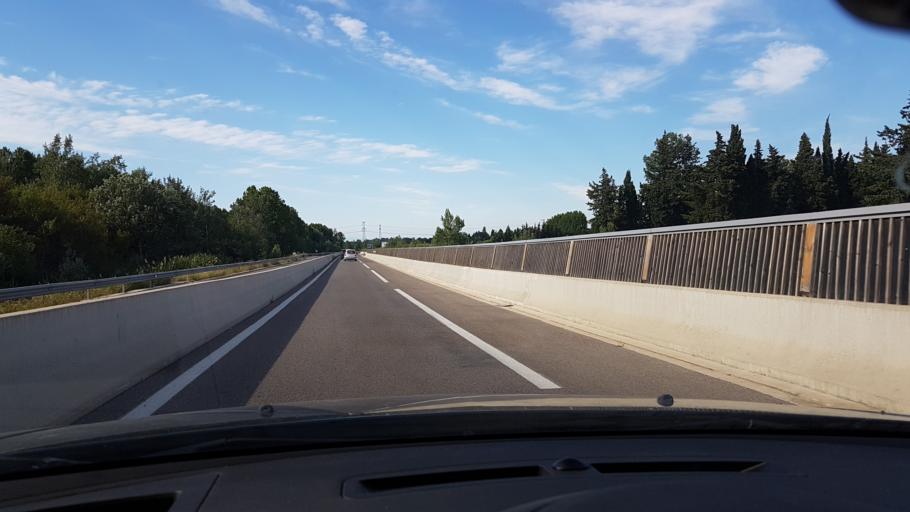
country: FR
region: Provence-Alpes-Cote d'Azur
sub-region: Departement des Bouches-du-Rhone
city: Rognonas
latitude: 43.9034
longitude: 4.7873
